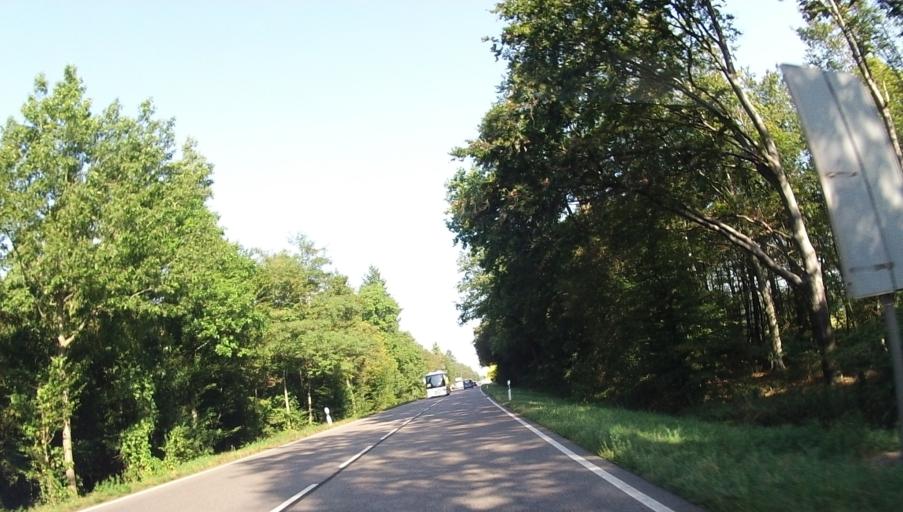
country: DE
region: Baden-Wuerttemberg
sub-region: Karlsruhe Region
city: Iffezheim
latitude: 48.8057
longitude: 8.1403
